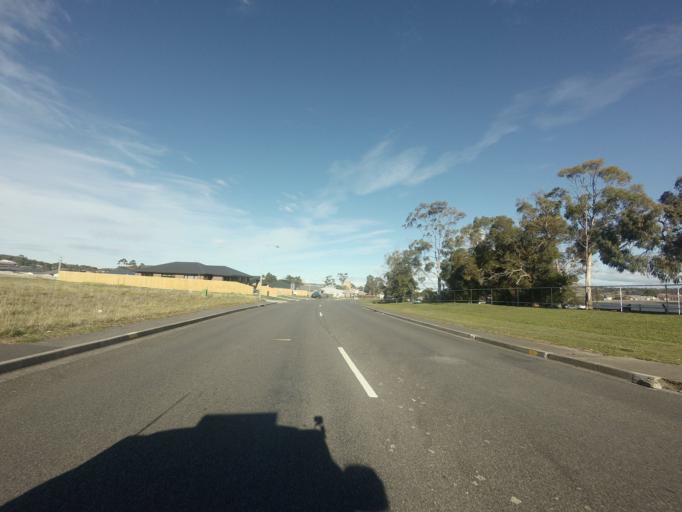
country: AU
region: Tasmania
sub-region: Clarence
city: Rokeby
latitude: -42.8971
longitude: 147.4470
